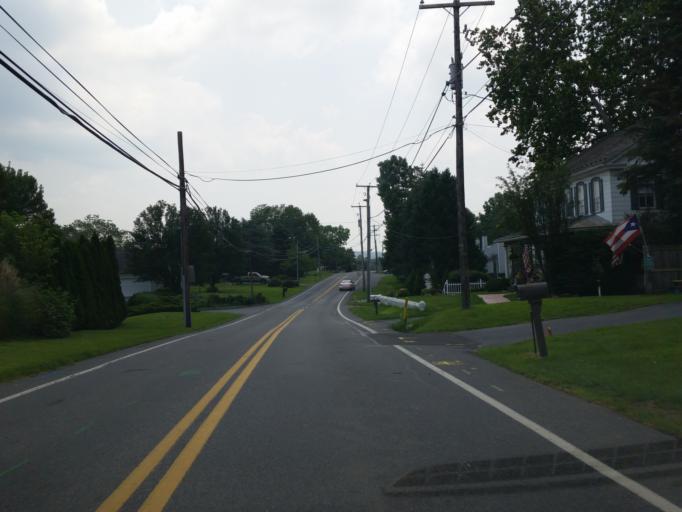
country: US
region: Pennsylvania
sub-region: Dauphin County
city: Palmdale
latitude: 40.2953
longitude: -76.6041
